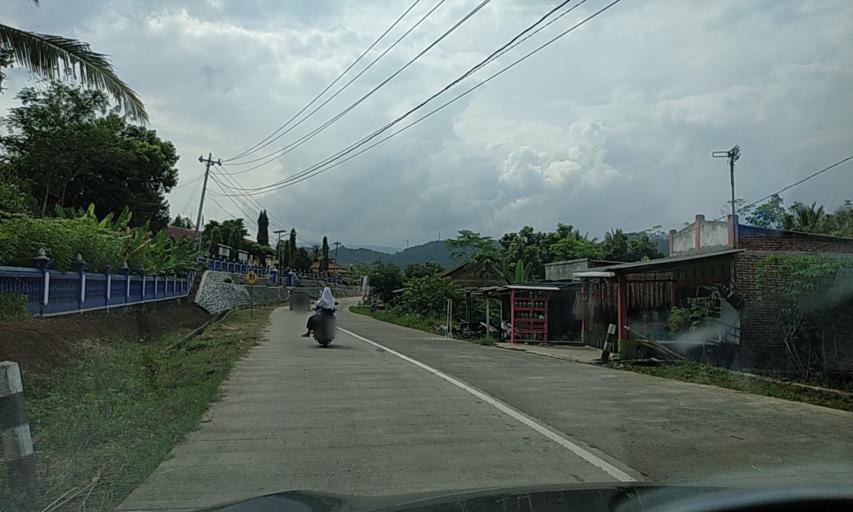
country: ID
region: Central Java
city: Winangun
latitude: -7.3497
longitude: 108.7086
